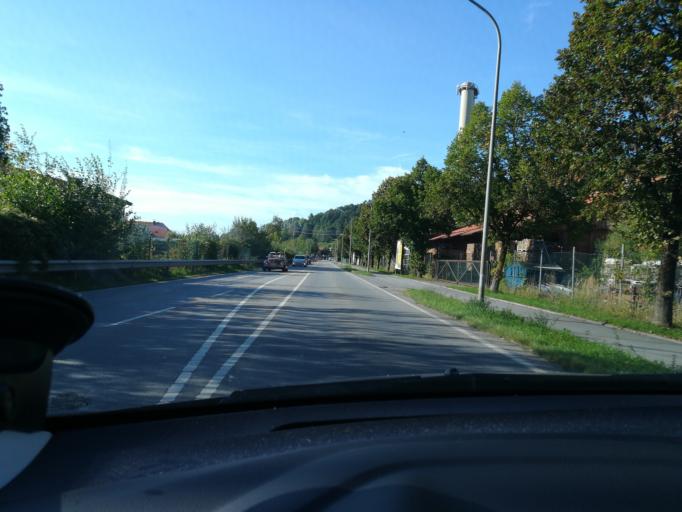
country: DE
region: Bavaria
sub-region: Upper Bavaria
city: Hausham
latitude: 47.7508
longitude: 11.8402
